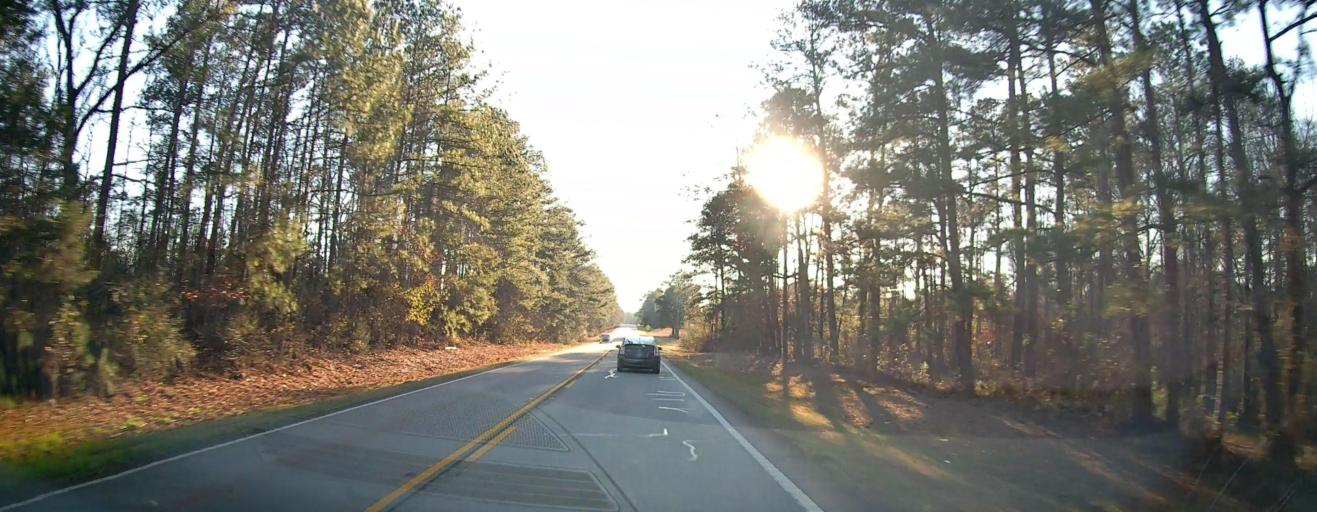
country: US
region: Georgia
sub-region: Harris County
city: Pine Mountain
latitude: 32.8488
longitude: -84.8903
